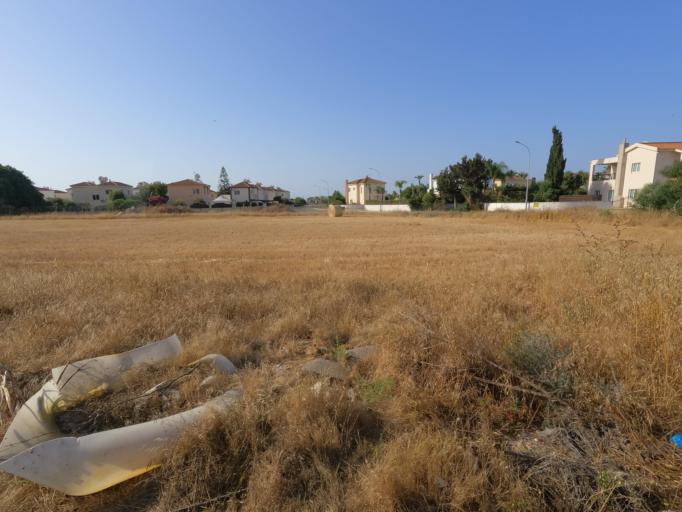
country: CY
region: Ammochostos
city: Liopetri
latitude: 34.9815
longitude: 33.9230
